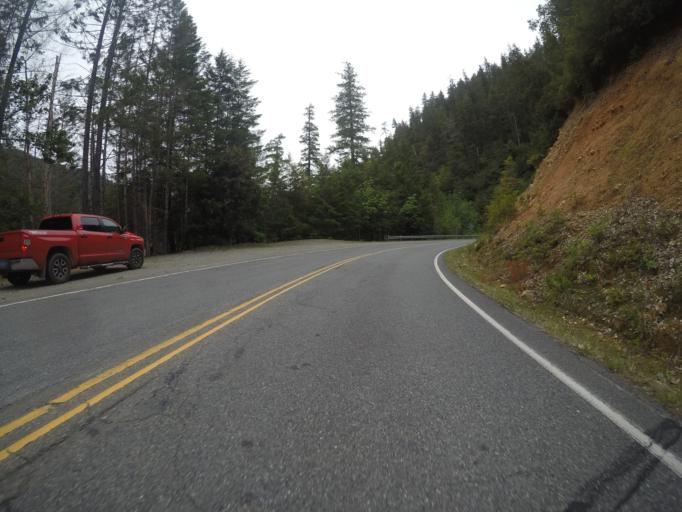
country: US
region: California
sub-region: Del Norte County
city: Bertsch-Oceanview
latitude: 41.7199
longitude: -123.9480
